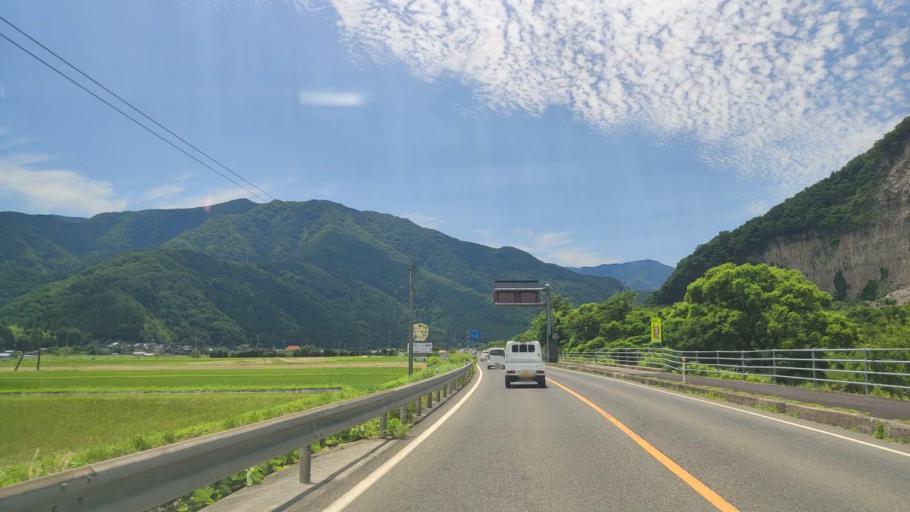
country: JP
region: Tottori
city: Tottori
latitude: 35.3654
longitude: 134.3691
